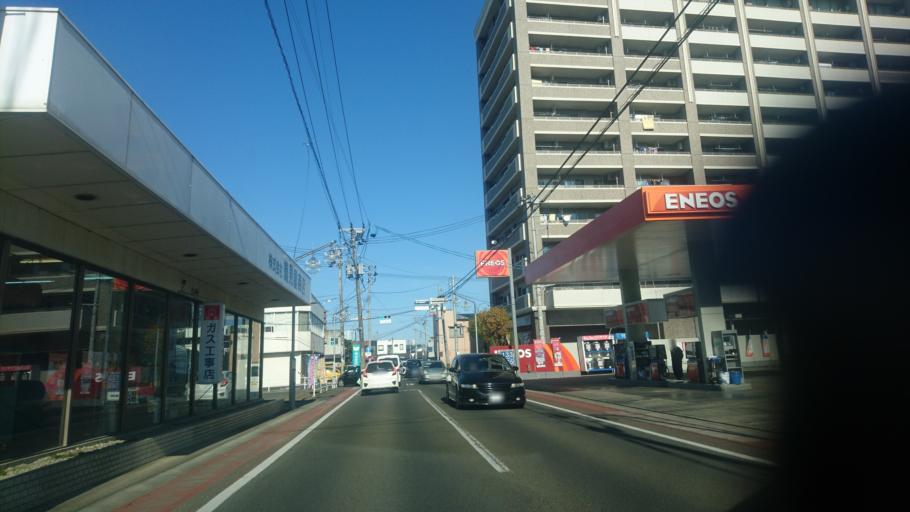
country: JP
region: Miyagi
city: Iwanuma
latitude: 38.1700
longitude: 140.8860
